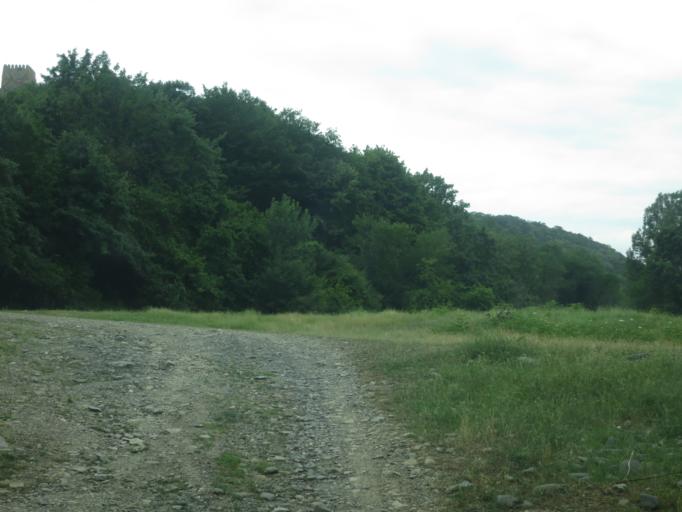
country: GE
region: Kakheti
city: Tsinandali
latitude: 42.0030
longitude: 45.6596
